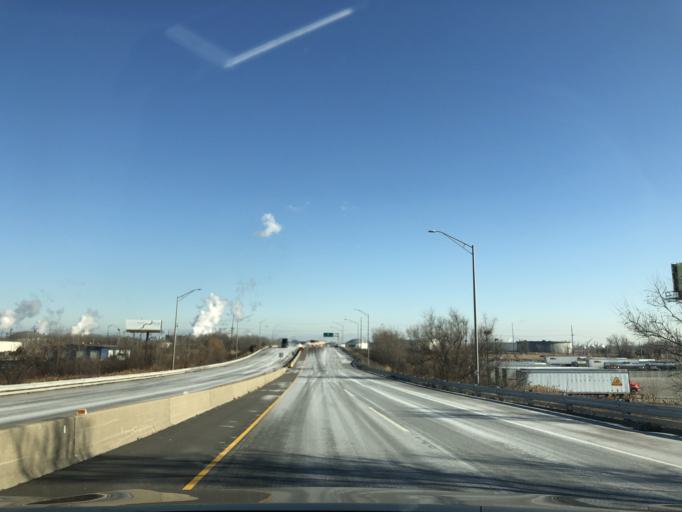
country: US
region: Indiana
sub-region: Lake County
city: Whiting
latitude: 41.6569
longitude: -87.5125
